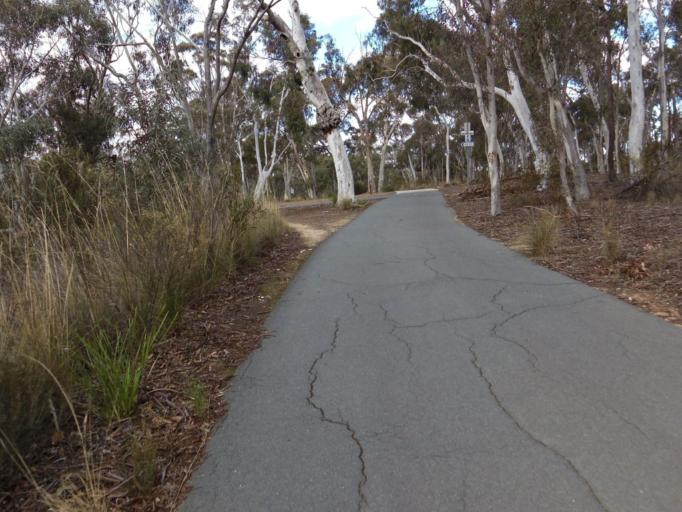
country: AU
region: Australian Capital Territory
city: Macquarie
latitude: -35.2512
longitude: 149.0958
